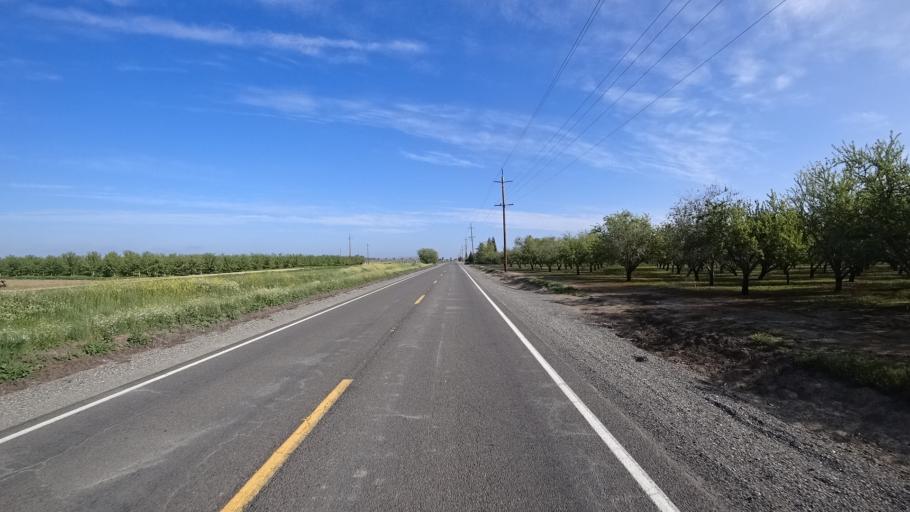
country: US
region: California
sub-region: Glenn County
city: Hamilton City
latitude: 39.5944
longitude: -122.0076
